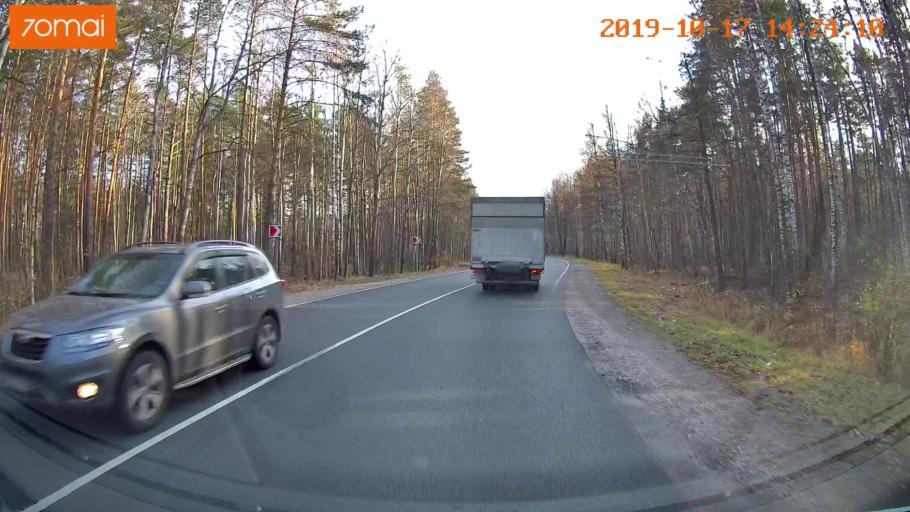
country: RU
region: Moskovskaya
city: Radovitskiy
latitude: 55.0116
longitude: 39.9654
